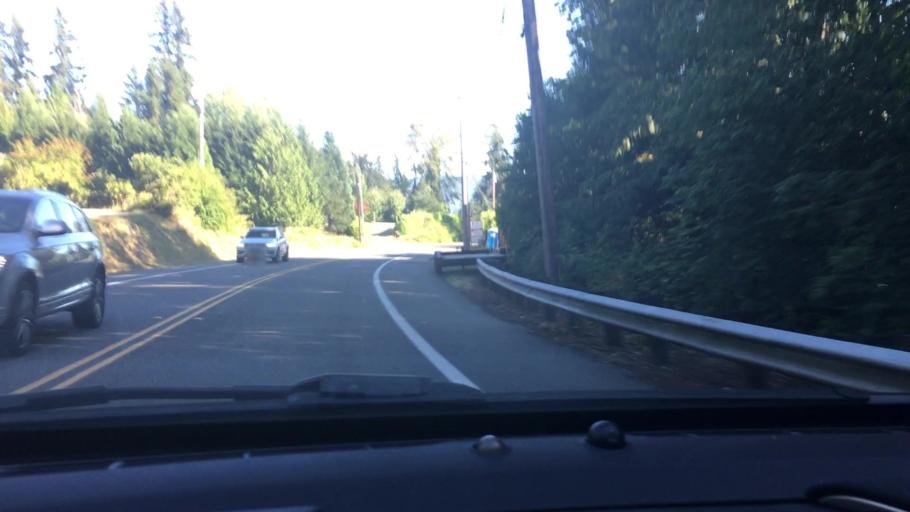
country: US
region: Washington
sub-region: King County
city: West Lake Sammamish
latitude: 47.5865
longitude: -122.0827
